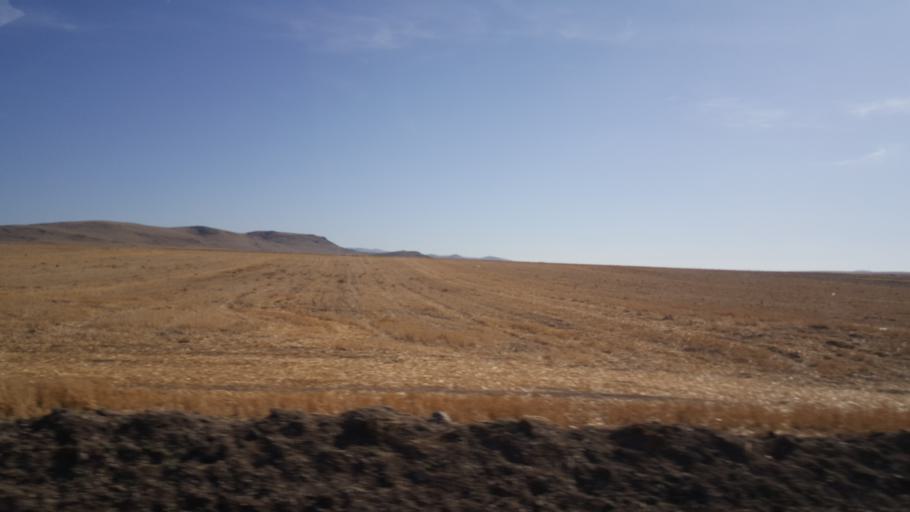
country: TR
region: Ankara
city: Yenice
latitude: 39.3521
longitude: 32.7770
